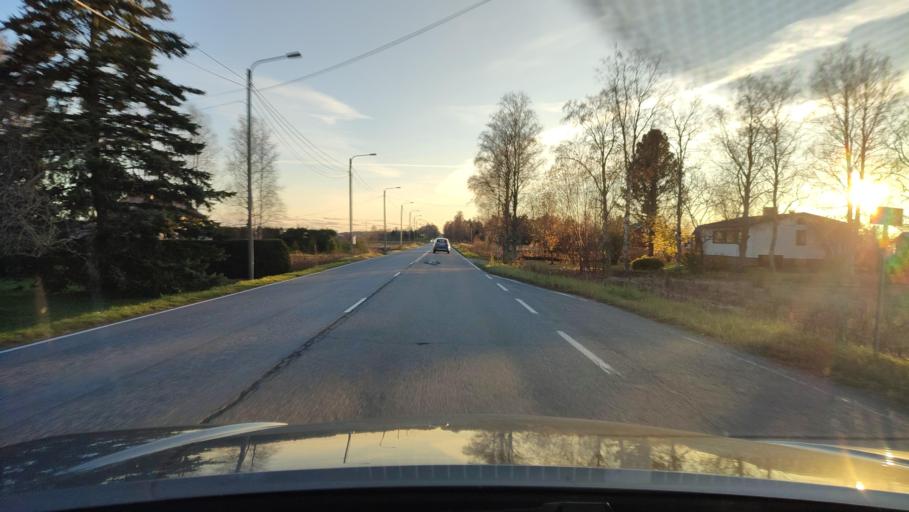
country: FI
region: Ostrobothnia
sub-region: Sydosterbotten
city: Naerpes
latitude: 62.5113
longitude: 21.3611
